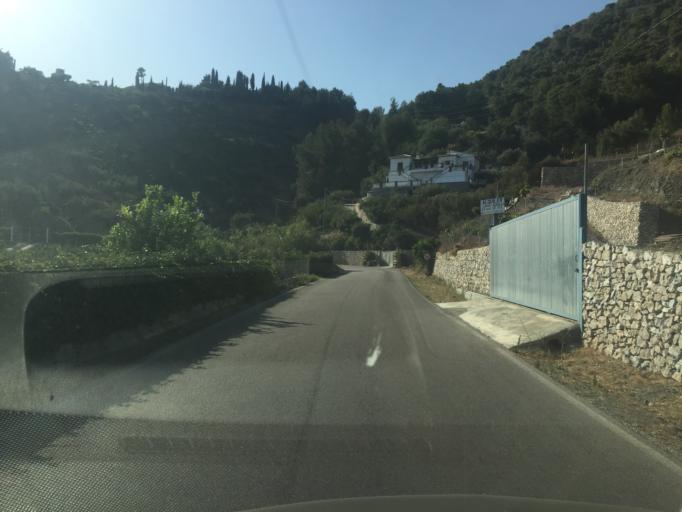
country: ES
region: Andalusia
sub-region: Provincia de Malaga
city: Frigiliana
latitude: 36.8048
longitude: -3.9160
